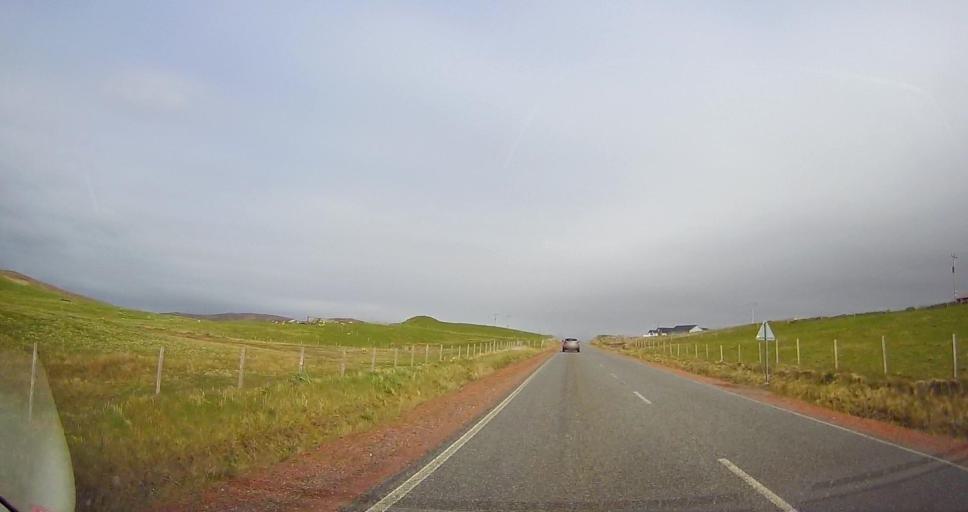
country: GB
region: Scotland
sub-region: Shetland Islands
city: Sandwick
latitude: 60.1179
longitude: -1.2915
